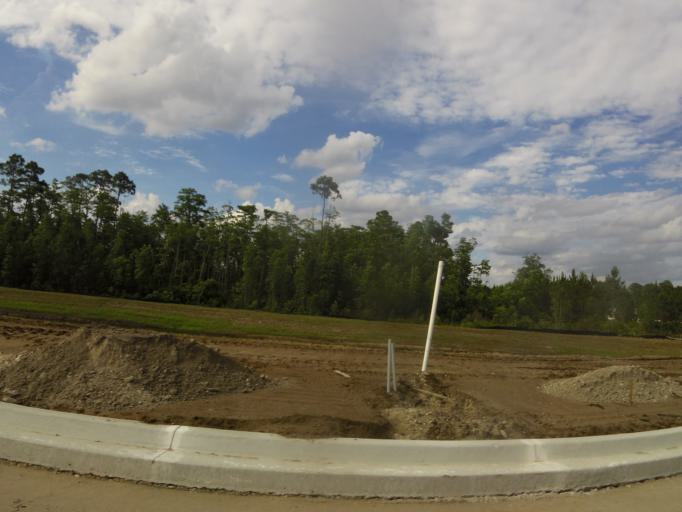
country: US
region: Florida
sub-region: Saint Johns County
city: Palm Valley
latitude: 30.1795
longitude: -81.5045
